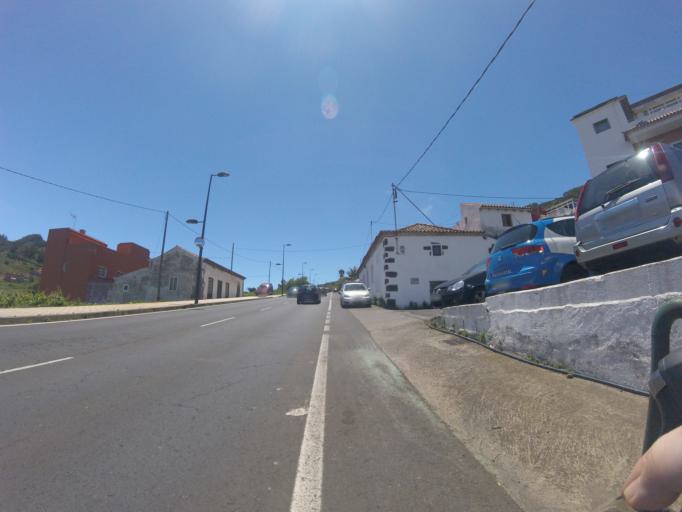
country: ES
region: Canary Islands
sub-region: Provincia de Santa Cruz de Tenerife
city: Tegueste
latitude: 28.5159
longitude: -16.3180
